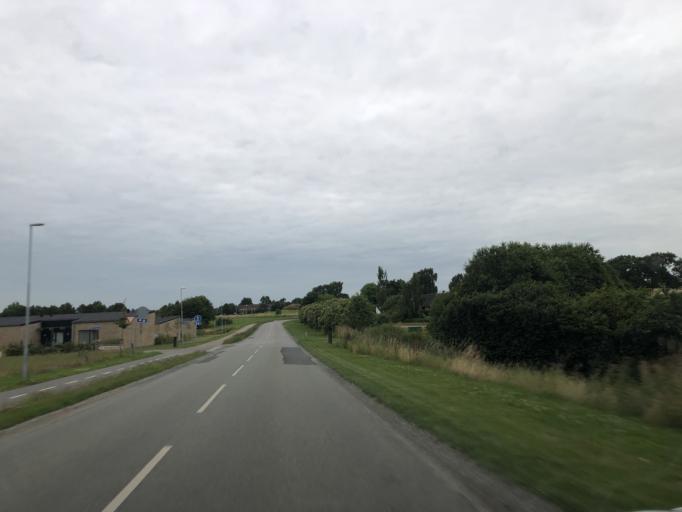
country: DK
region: South Denmark
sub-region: Vejle Kommune
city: Jelling
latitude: 55.7453
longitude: 9.4134
